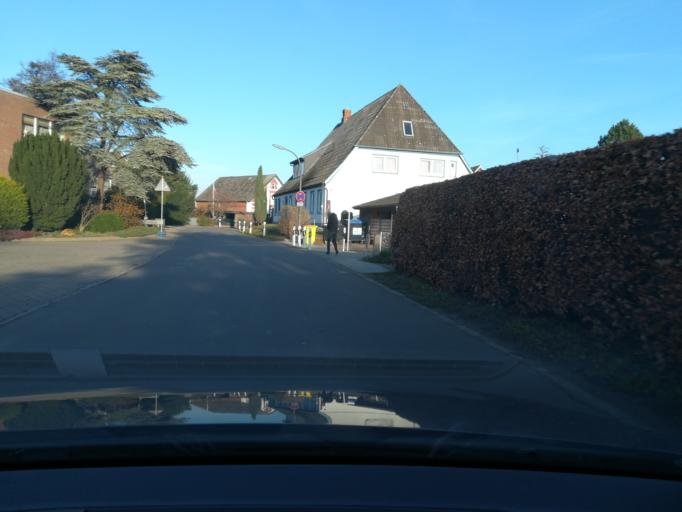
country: DE
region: Lower Saxony
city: Stelle
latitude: 53.4436
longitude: 10.1247
